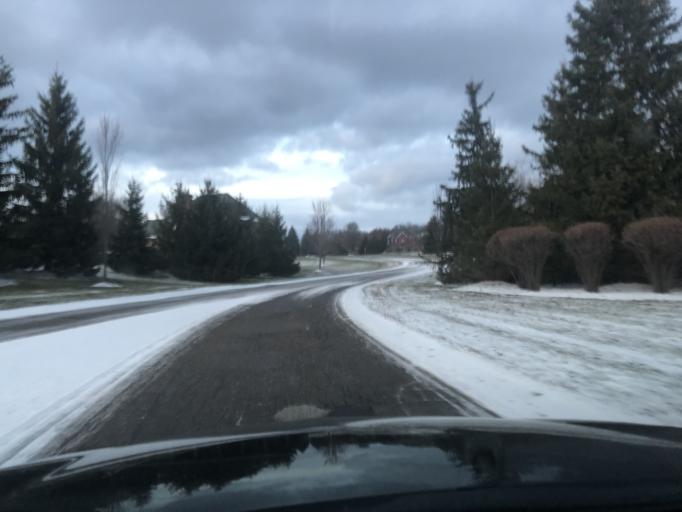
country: US
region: Michigan
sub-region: Oakland County
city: Milford
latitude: 42.5788
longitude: -83.6492
